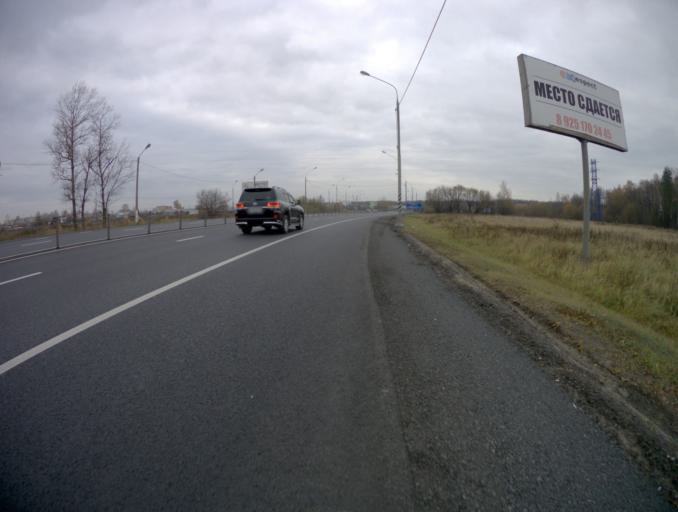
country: RU
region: Moskovskaya
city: Malaya Dubna
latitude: 55.8724
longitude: 38.9631
